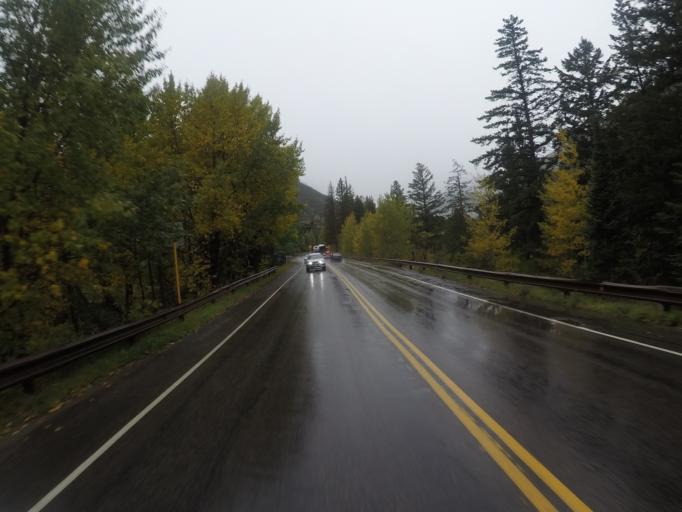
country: US
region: Colorado
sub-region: Pitkin County
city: Aspen
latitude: 39.1843
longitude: -106.8552
